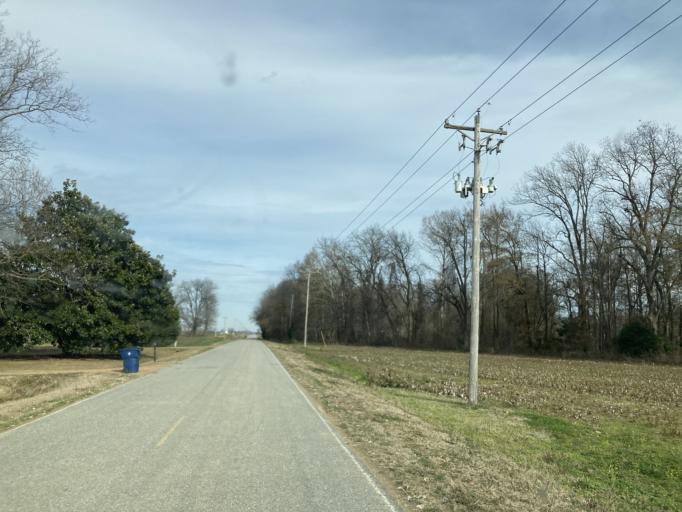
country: US
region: Mississippi
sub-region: Humphreys County
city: Belzoni
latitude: 33.0670
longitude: -90.6154
